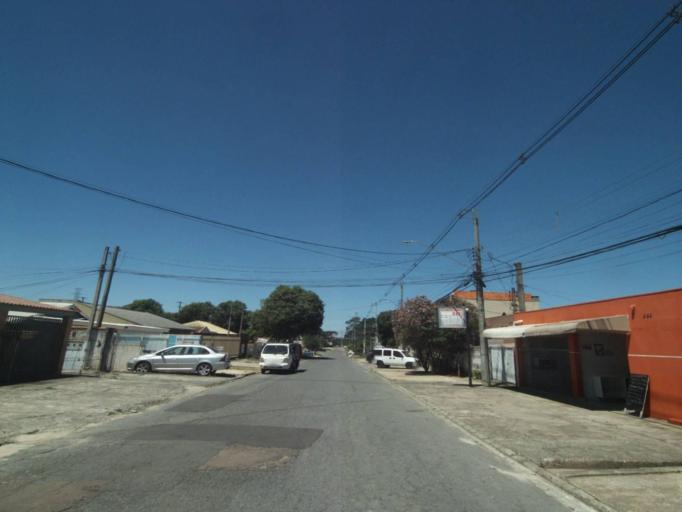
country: BR
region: Parana
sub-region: Curitiba
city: Curitiba
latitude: -25.4812
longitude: -49.3457
